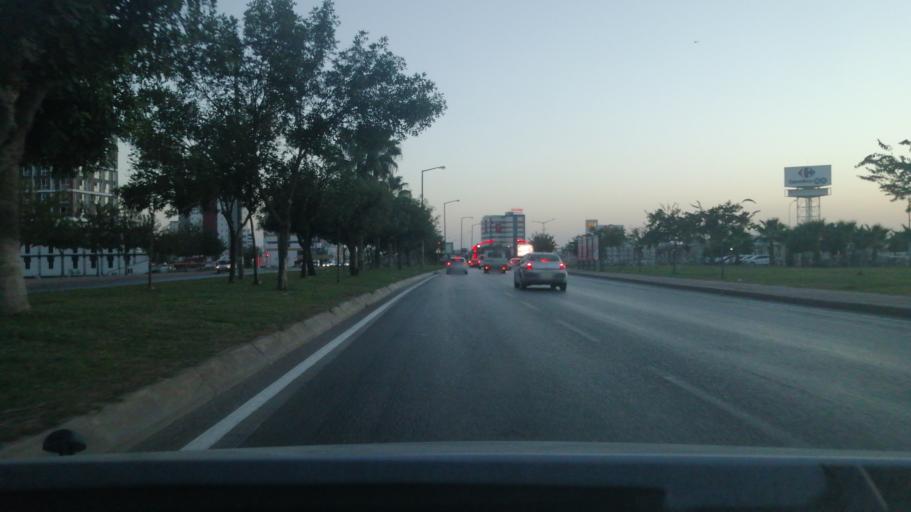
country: TR
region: Adana
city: Seyhan
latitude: 37.0175
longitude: 35.2516
